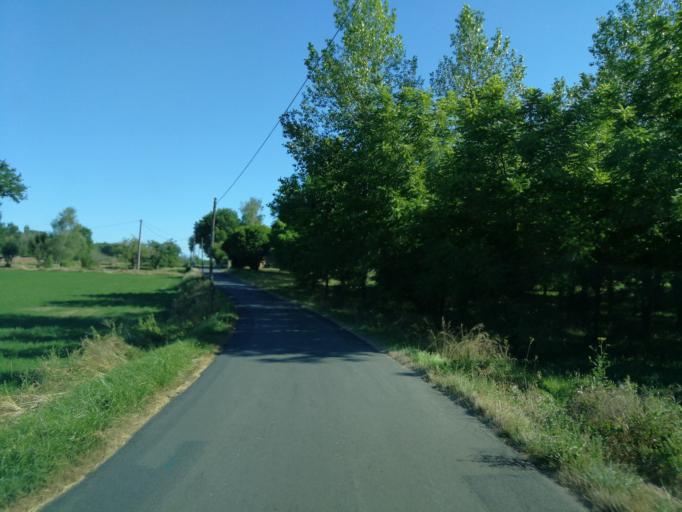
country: FR
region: Aquitaine
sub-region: Departement de la Dordogne
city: Eyvigues-et-Eybenes
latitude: 44.8346
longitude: 1.3600
